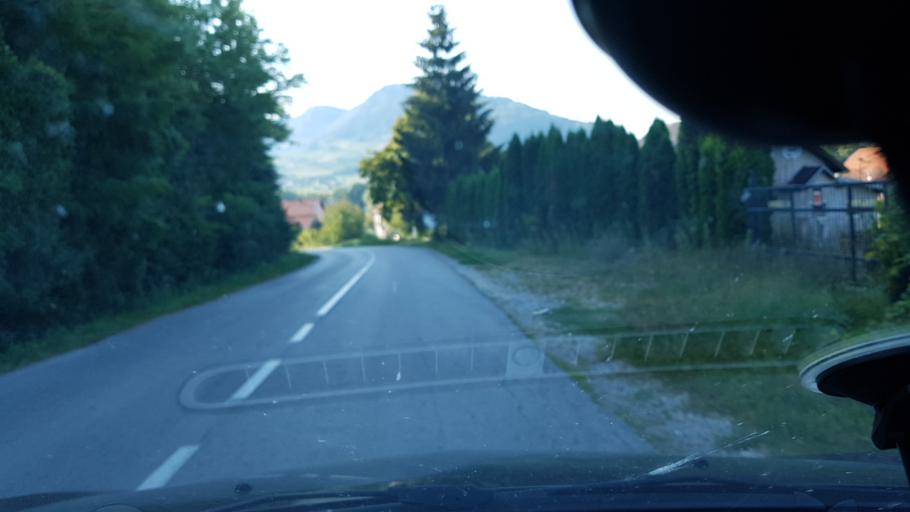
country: SI
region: Bistrica ob Sotli
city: Bistrica ob Sotli
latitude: 46.0356
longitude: 15.7323
